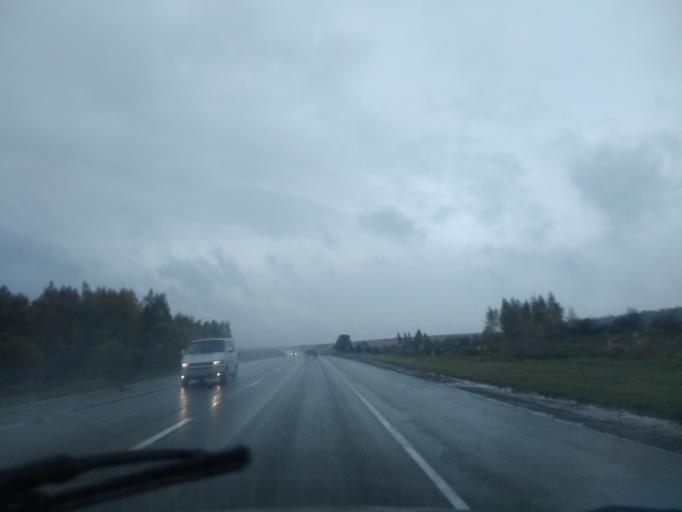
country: RU
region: Tula
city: Shchekino
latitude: 53.9854
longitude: 37.4723
